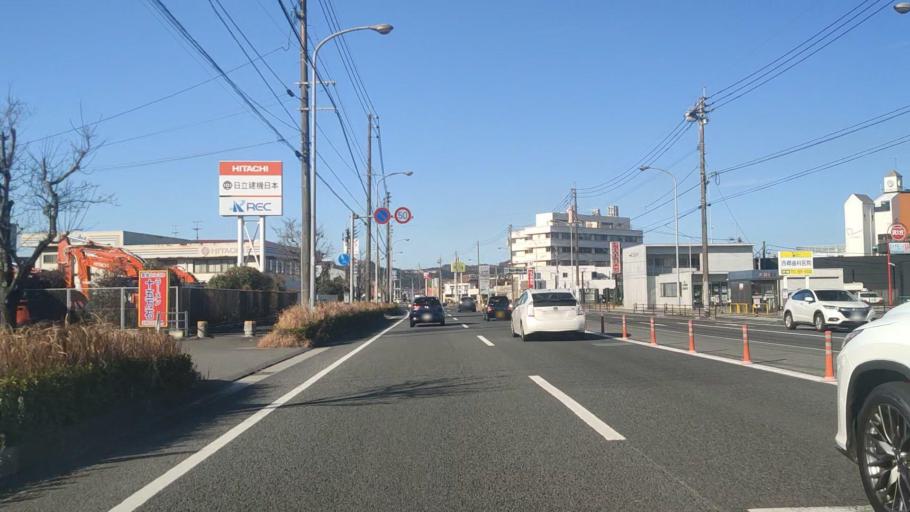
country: JP
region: Oita
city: Oita
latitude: 33.1525
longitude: 131.6563
